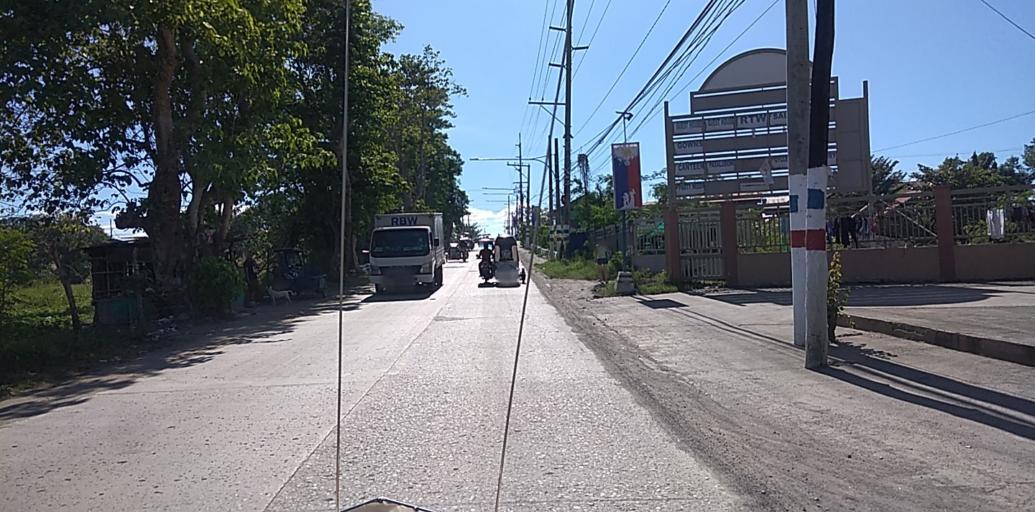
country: PH
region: Central Luzon
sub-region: Province of Pampanga
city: San Luis
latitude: 15.0458
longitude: 120.7869
